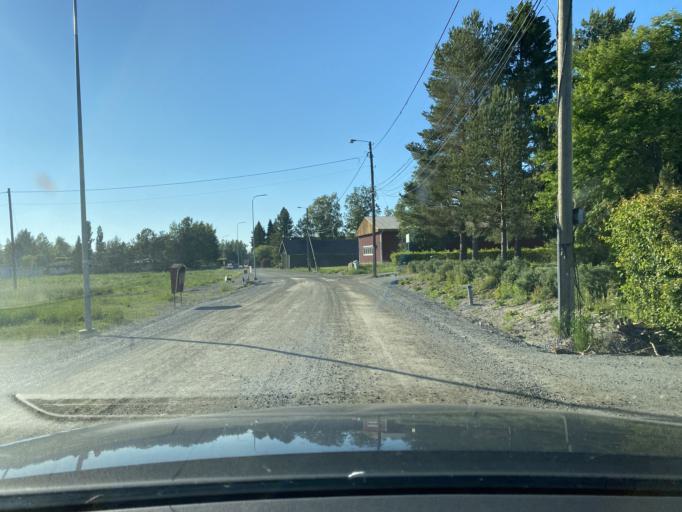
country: FI
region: Satakunta
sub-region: Pori
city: Huittinen
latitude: 61.1682
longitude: 22.7038
